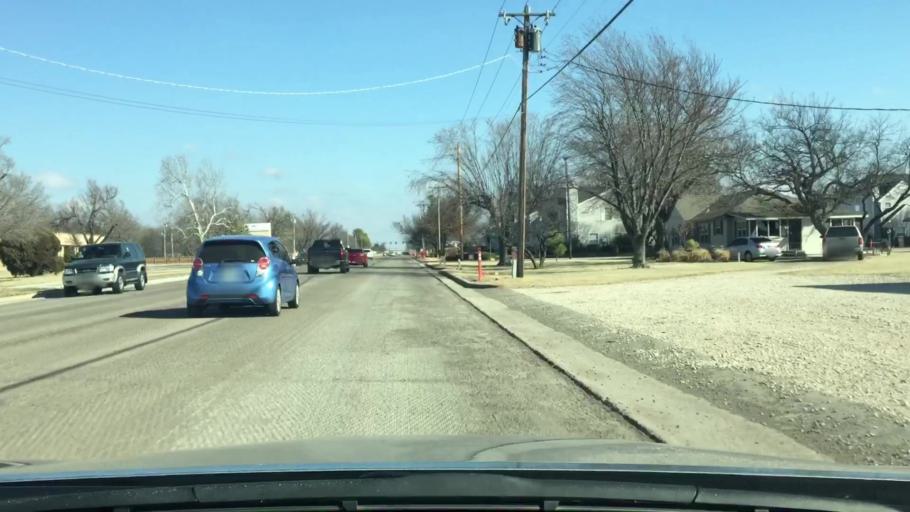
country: US
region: Oklahoma
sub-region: Cleveland County
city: Moore
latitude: 35.3772
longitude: -97.5178
